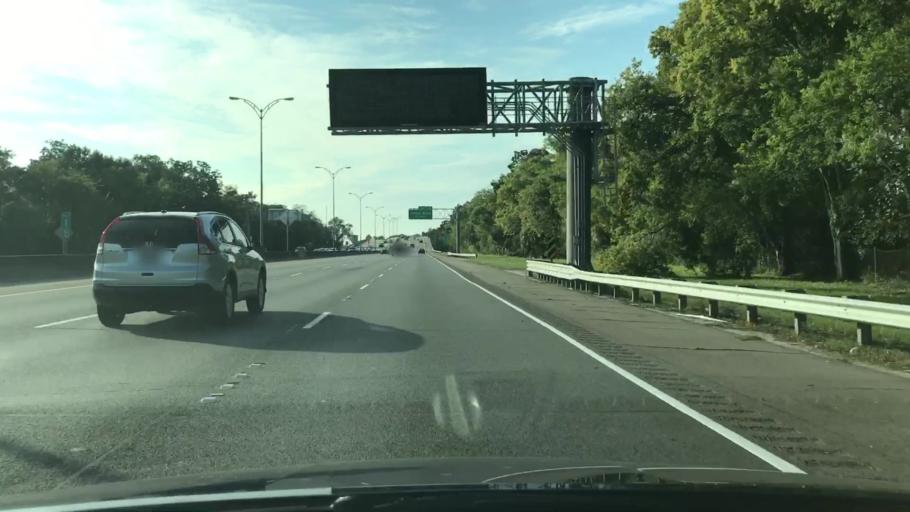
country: US
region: Louisiana
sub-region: Orleans Parish
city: New Orleans
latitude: 29.9940
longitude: -90.0954
